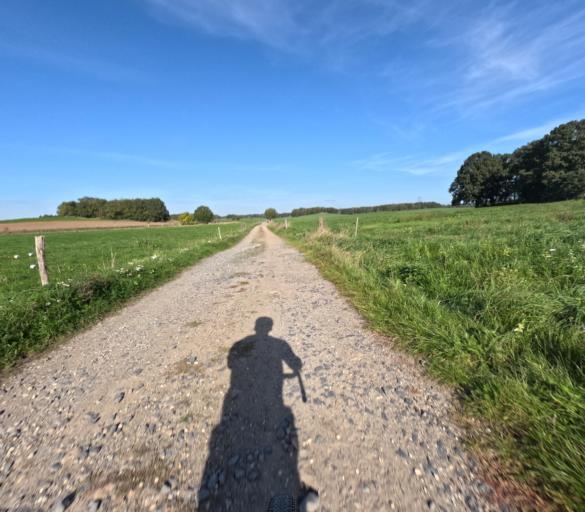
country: DE
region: Saxony
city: Radeburg
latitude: 51.1664
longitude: 13.7604
